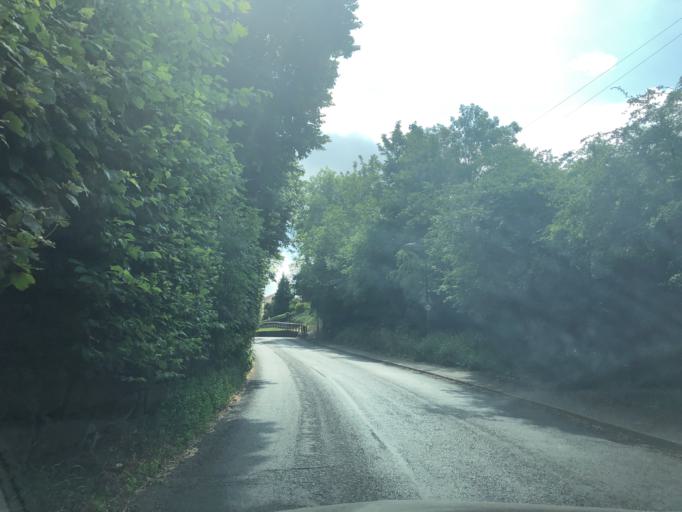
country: GB
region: England
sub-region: North Yorkshire
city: Stokesley
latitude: 54.4522
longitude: -1.2742
